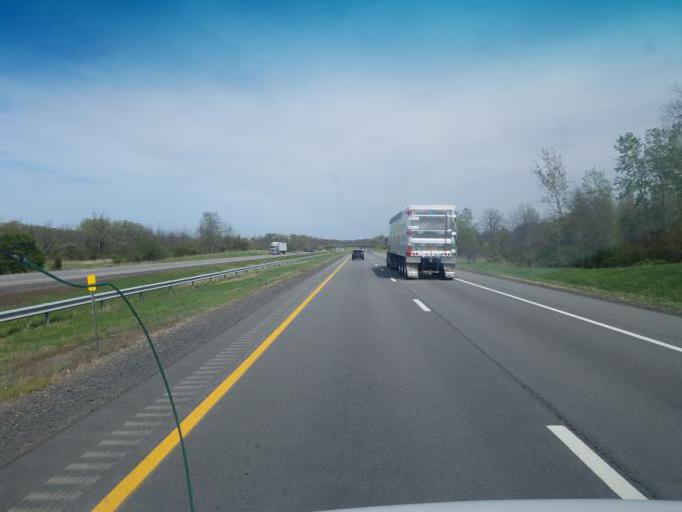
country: US
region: New York
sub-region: Livingston County
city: Caledonia
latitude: 43.0297
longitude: -77.8512
